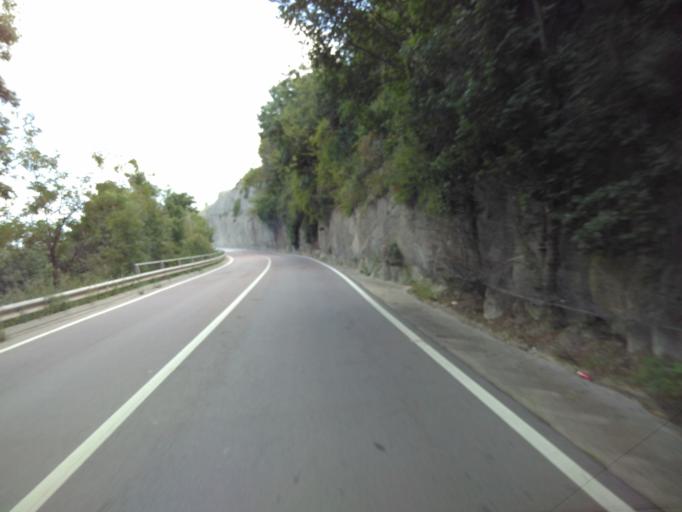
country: ES
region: Catalonia
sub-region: Provincia de Barcelona
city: Montesquiu
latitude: 42.0988
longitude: 2.2190
